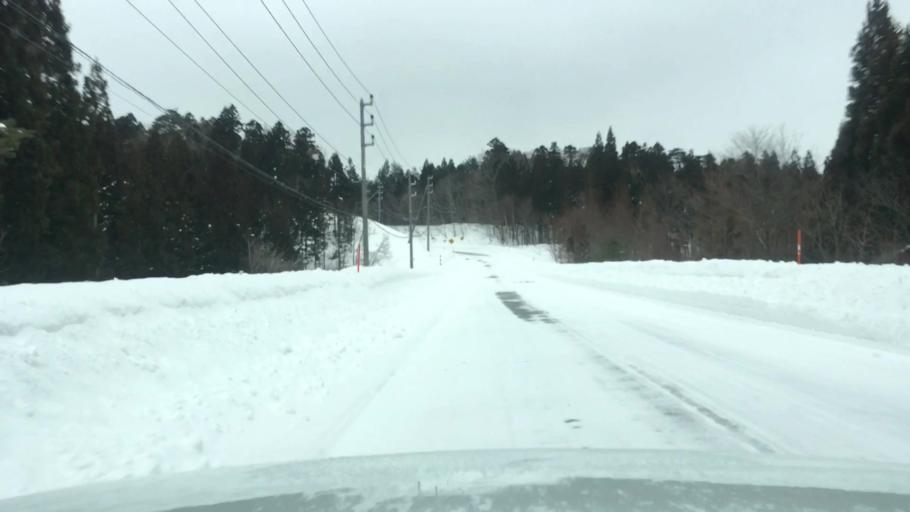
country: JP
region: Akita
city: Hanawa
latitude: 39.9978
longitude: 140.9900
